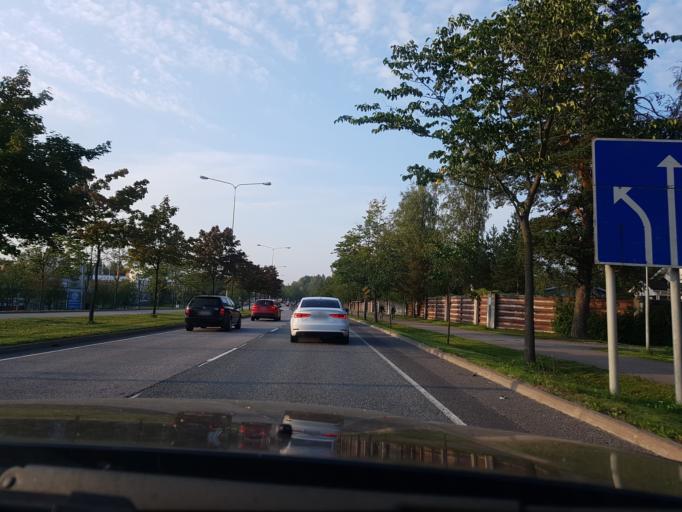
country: FI
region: Uusimaa
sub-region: Helsinki
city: Tuusula
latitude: 60.3866
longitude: 25.0254
